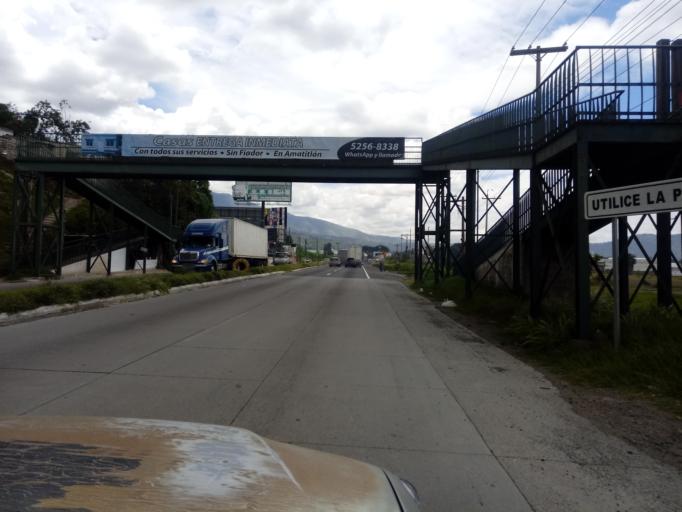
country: GT
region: Guatemala
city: Amatitlan
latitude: 14.4578
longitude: -90.6433
